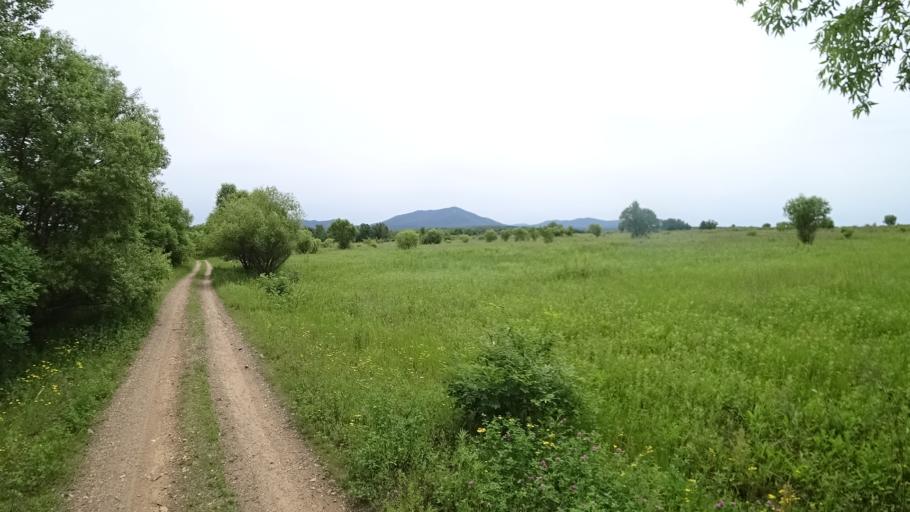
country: RU
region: Primorskiy
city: Arsen'yev
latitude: 44.1826
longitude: 133.3192
